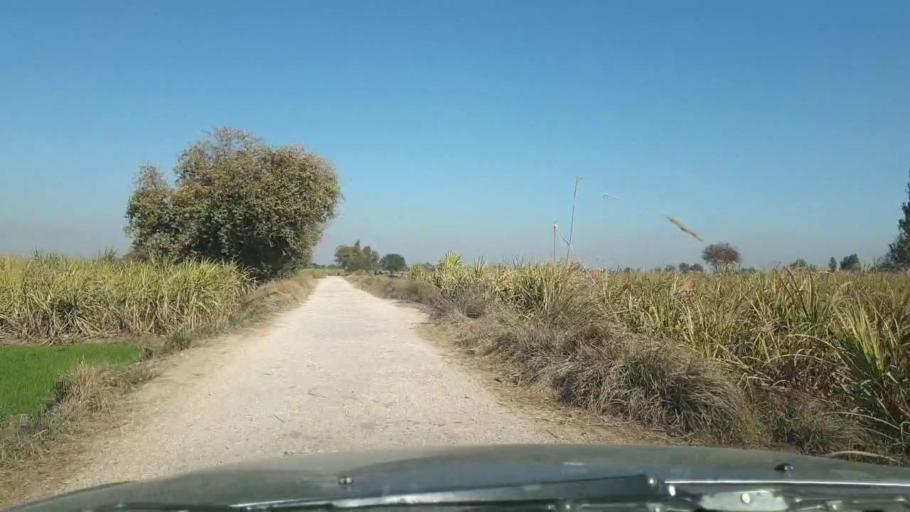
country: PK
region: Sindh
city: Ghotki
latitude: 28.0496
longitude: 69.2411
